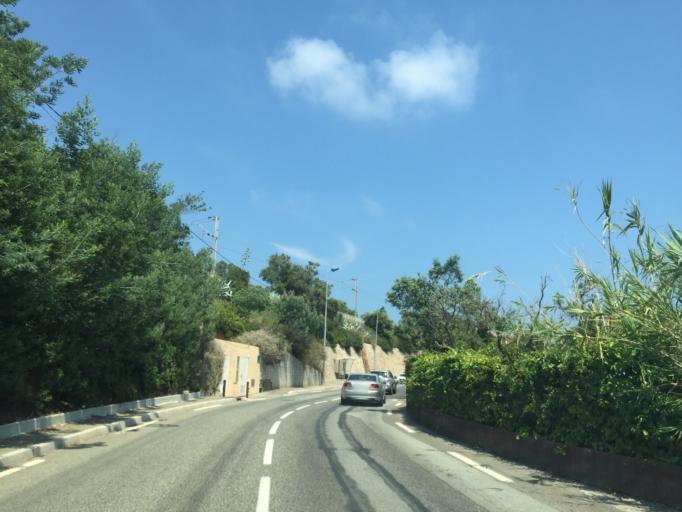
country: FR
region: Provence-Alpes-Cote d'Azur
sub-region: Departement des Alpes-Maritimes
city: Theoule-sur-Mer
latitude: 43.4289
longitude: 6.8861
